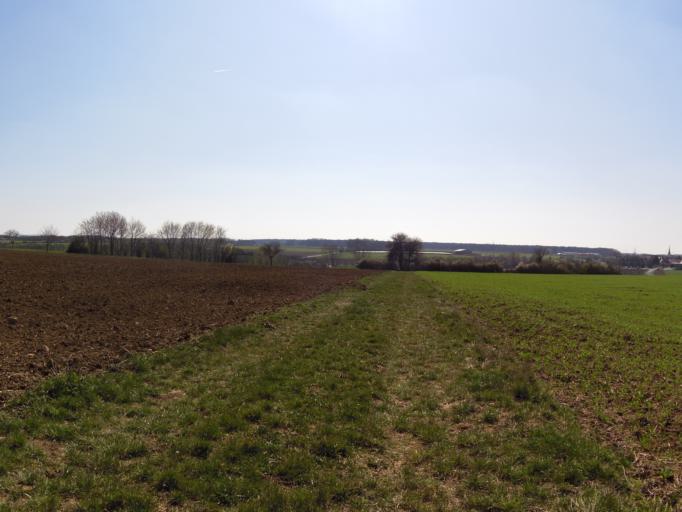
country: DE
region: Bavaria
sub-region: Regierungsbezirk Unterfranken
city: Biebelried
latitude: 49.7375
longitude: 10.0979
